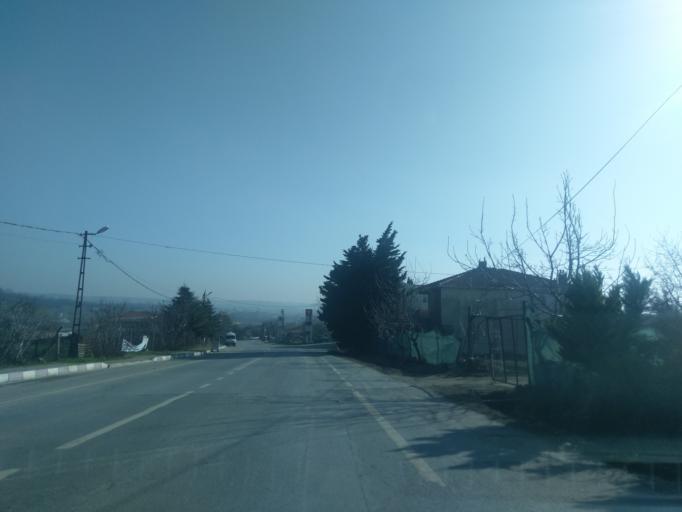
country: TR
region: Istanbul
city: Catalca
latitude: 41.1168
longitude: 28.4503
